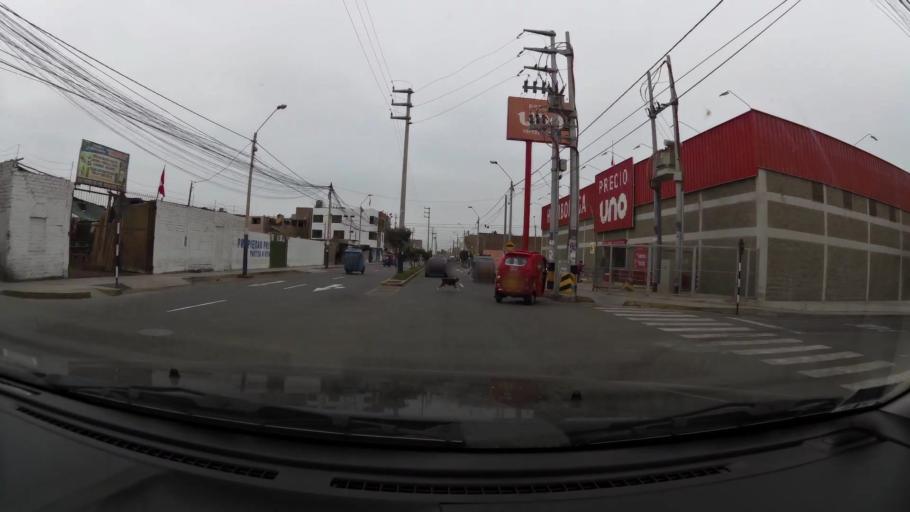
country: PE
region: Ica
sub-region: Provincia de Pisco
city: Pisco
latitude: -13.7157
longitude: -76.2040
